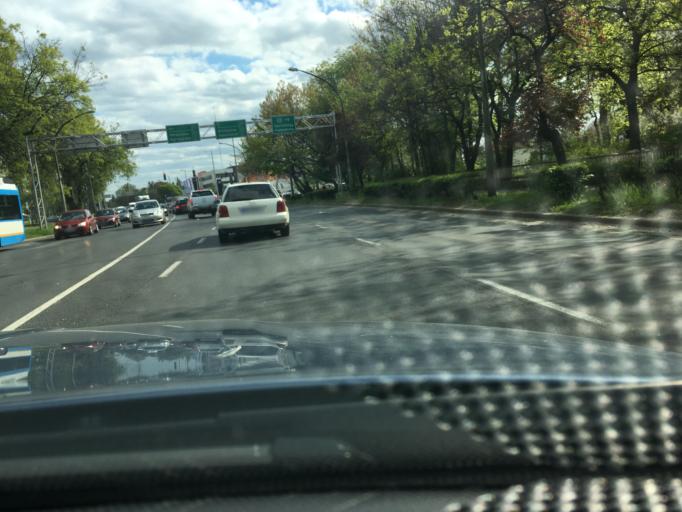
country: HU
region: Hajdu-Bihar
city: Debrecen
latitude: 47.5428
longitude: 21.6096
